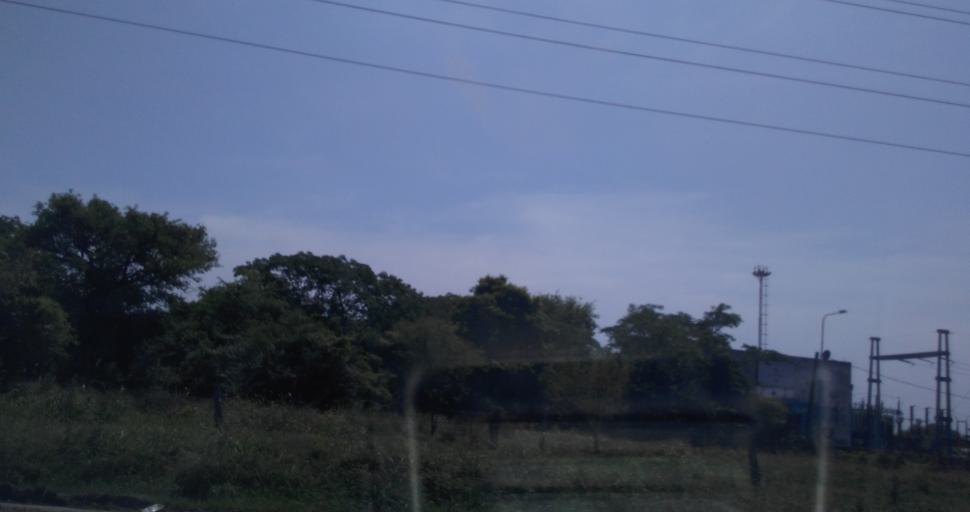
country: AR
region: Chaco
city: Fontana
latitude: -27.4001
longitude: -59.0030
